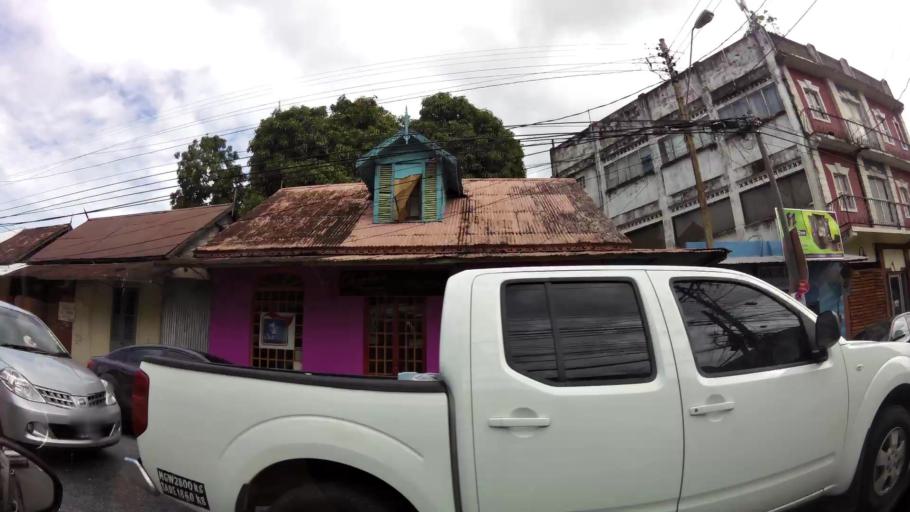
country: TT
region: City of Port of Spain
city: Port-of-Spain
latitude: 10.6615
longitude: -61.5182
